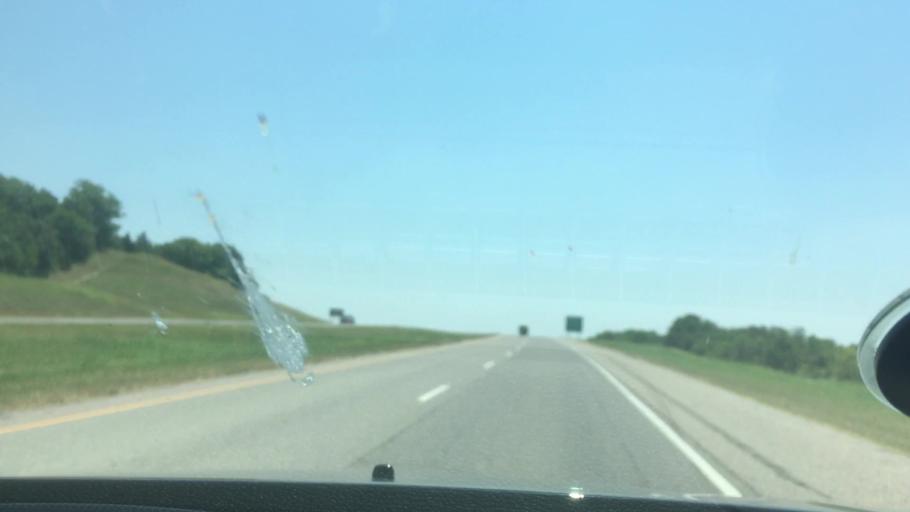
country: US
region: Oklahoma
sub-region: Pontotoc County
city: Ada
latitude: 34.7319
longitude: -96.6405
